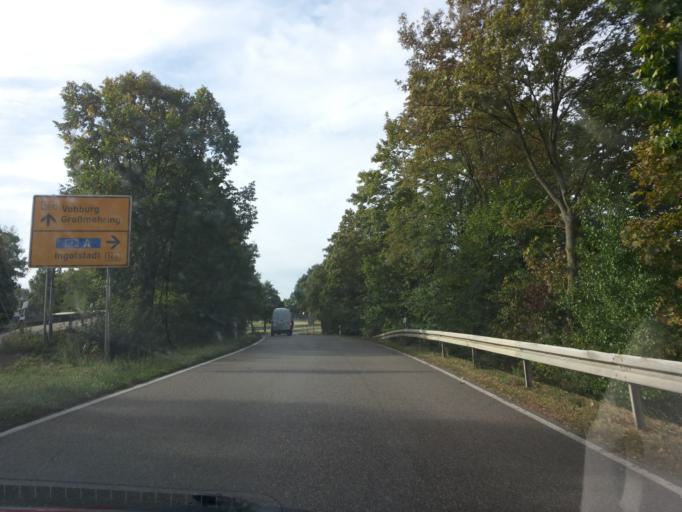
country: DE
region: Bavaria
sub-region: Upper Bavaria
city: Lenting
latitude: 48.7767
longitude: 11.4772
